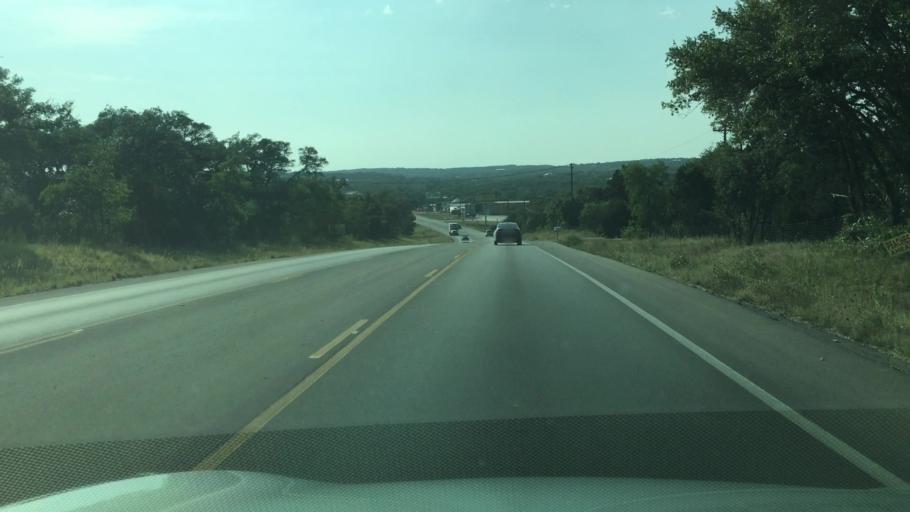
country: US
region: Texas
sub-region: Hays County
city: Wimberley
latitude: 29.9272
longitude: -98.0667
